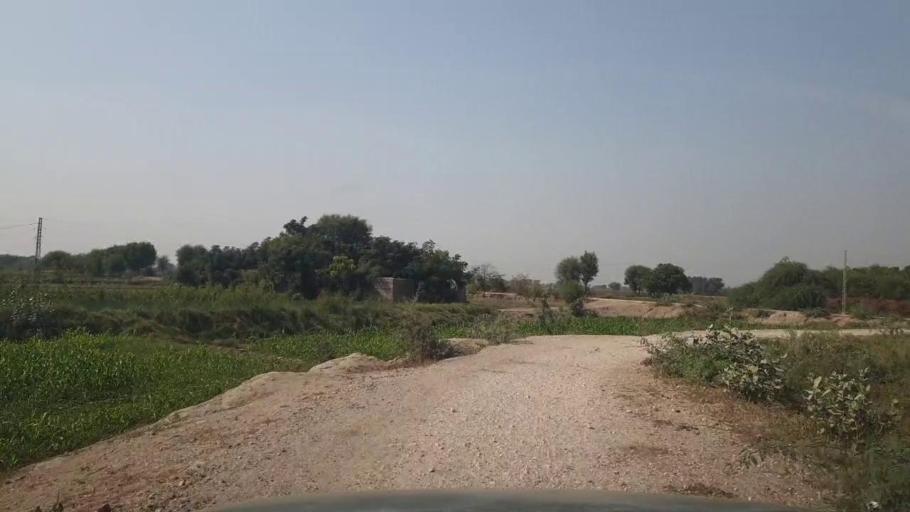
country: PK
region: Sindh
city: Bhit Shah
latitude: 25.7392
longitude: 68.5001
